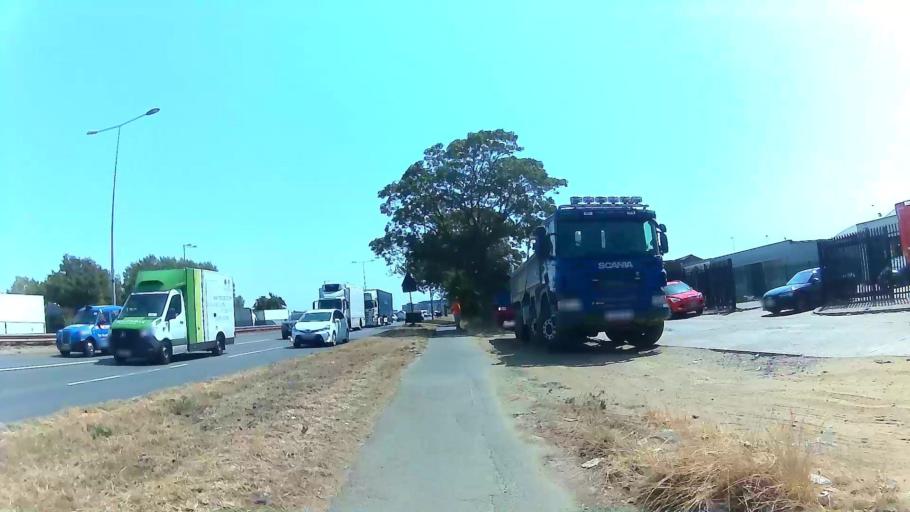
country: GB
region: England
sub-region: Greater London
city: Becontree
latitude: 51.5320
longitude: 0.1191
